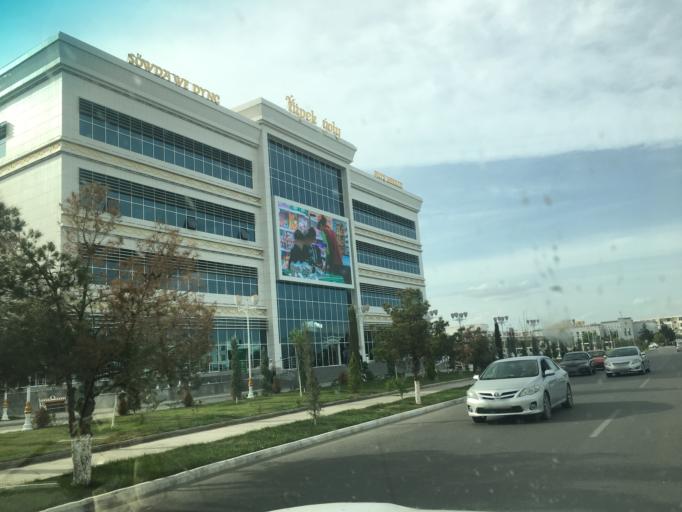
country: TM
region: Mary
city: Mary
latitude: 37.5924
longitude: 61.8371
